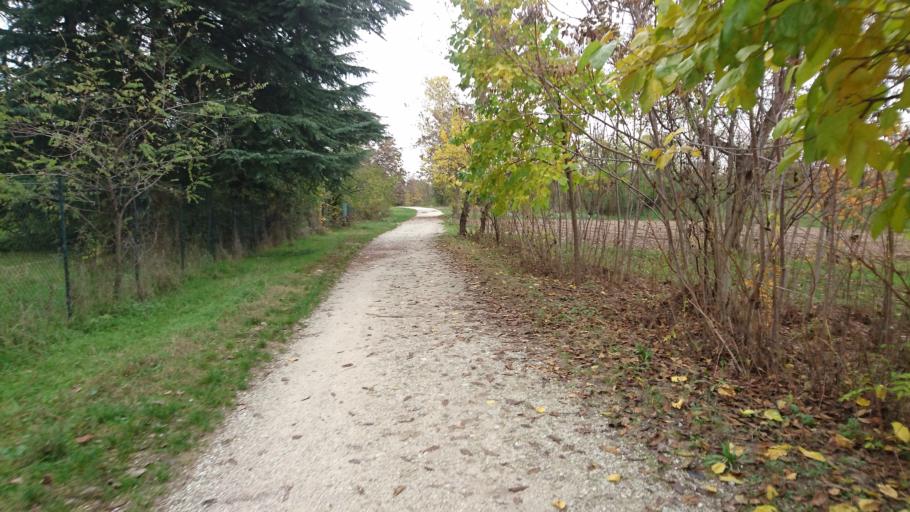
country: IT
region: Piedmont
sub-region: Provincia di Cuneo
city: Cuneo
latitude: 44.3843
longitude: 7.5523
